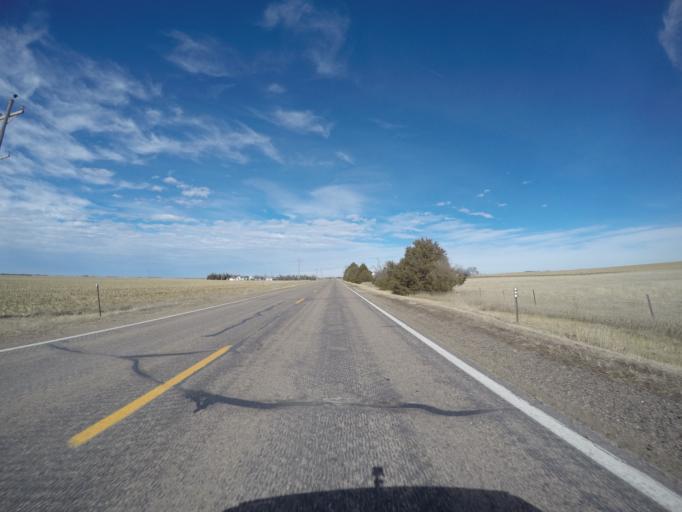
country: US
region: Nebraska
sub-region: Franklin County
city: Franklin
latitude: 40.1725
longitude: -98.9526
